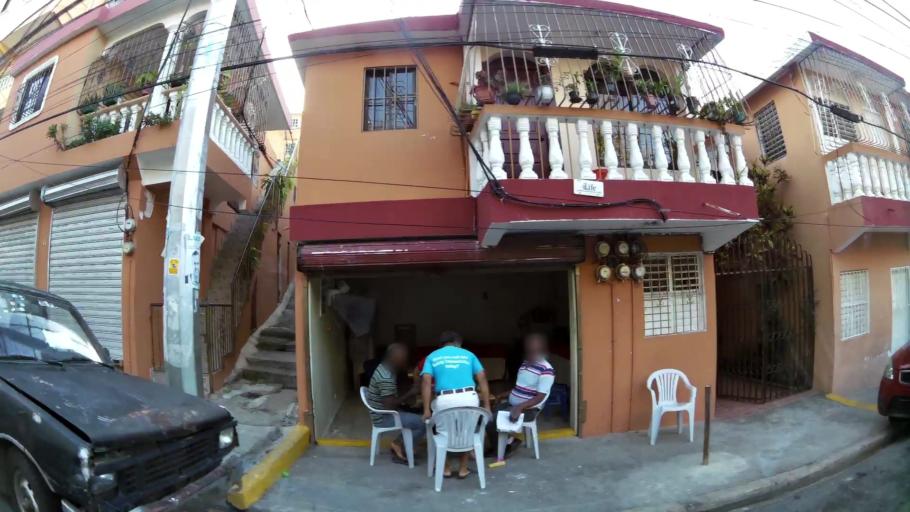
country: DO
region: Nacional
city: Santo Domingo
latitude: 18.4880
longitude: -69.9683
